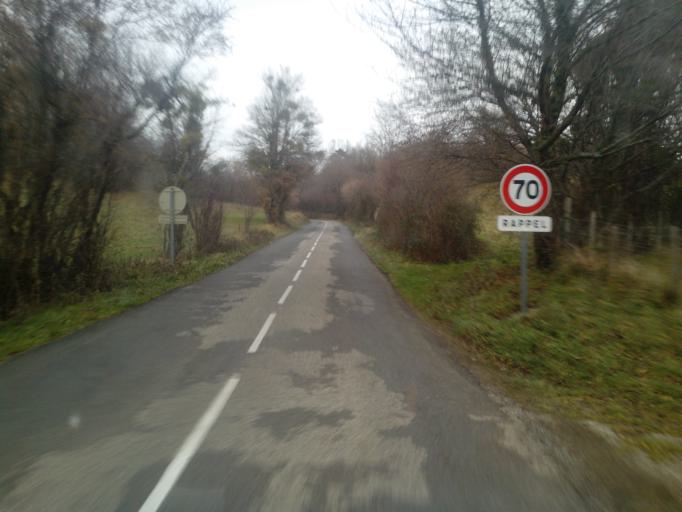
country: FR
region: Midi-Pyrenees
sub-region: Departement de l'Ariege
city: Foix
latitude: 43.0140
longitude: 1.5208
